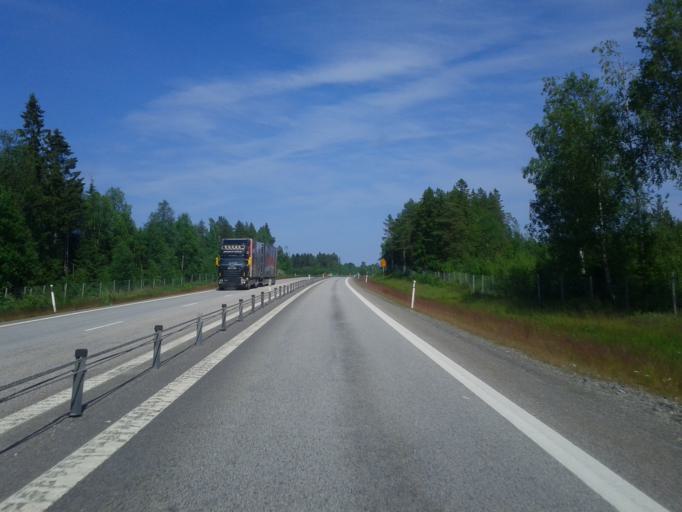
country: SE
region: Vaesterbotten
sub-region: Umea Kommun
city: Hoernefors
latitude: 63.6352
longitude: 19.8973
